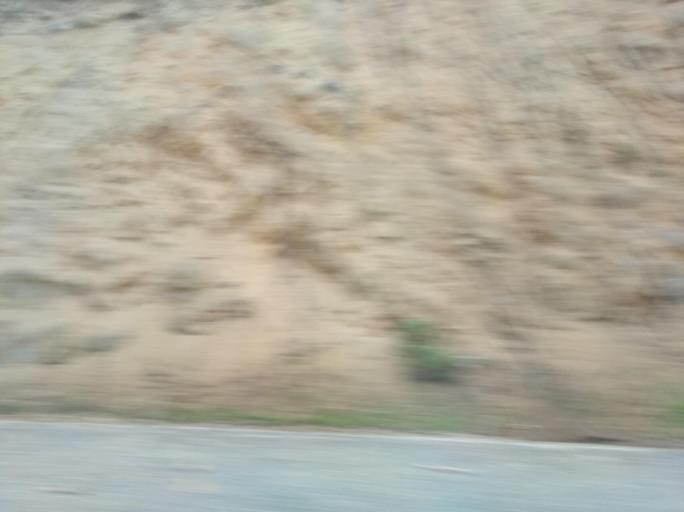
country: CL
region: Valparaiso
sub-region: Provincia de San Felipe
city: Llaillay
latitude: -33.0567
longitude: -71.0031
